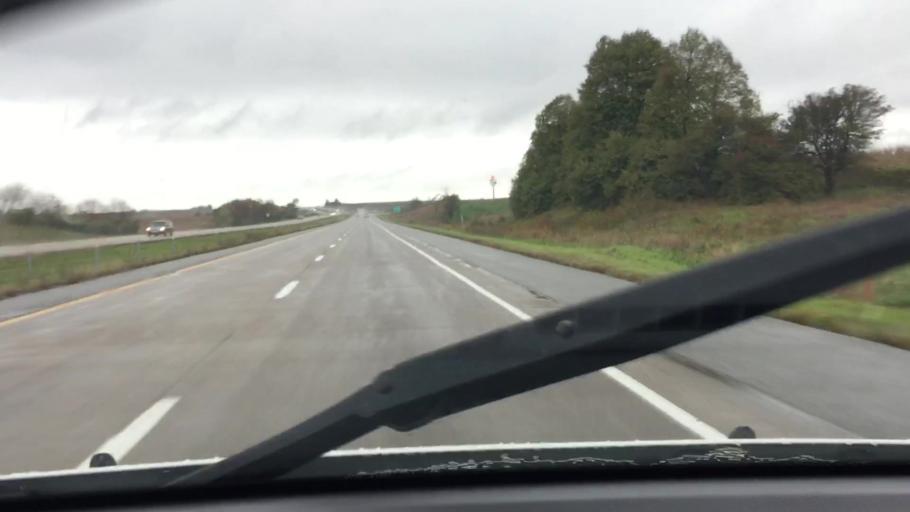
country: US
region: Iowa
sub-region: Poweshiek County
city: Brooklyn
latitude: 41.6963
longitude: -92.4322
